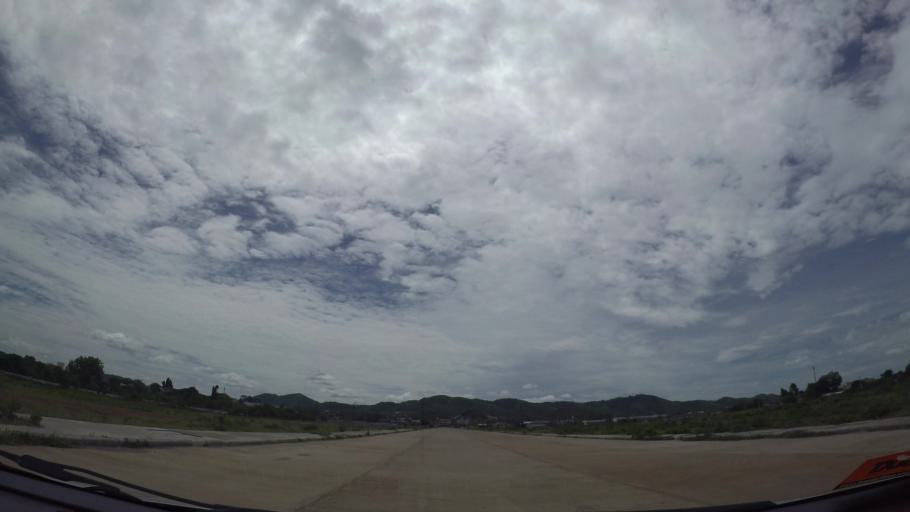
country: TH
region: Chon Buri
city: Sattahip
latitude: 12.6981
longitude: 100.8848
